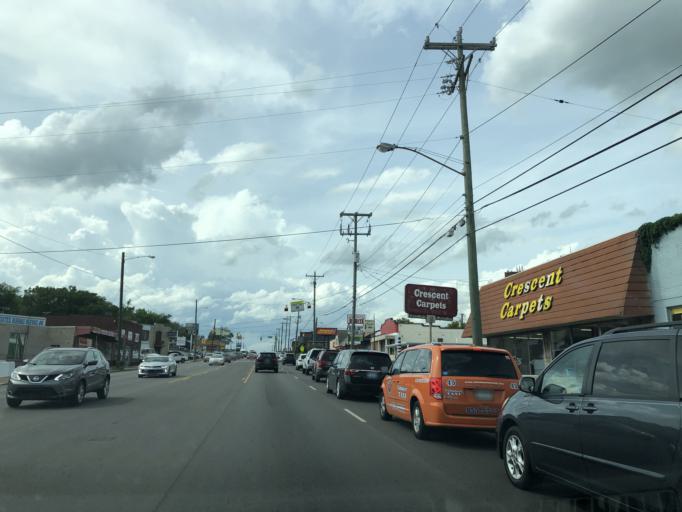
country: US
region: Tennessee
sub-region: Davidson County
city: Oak Hill
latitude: 36.1007
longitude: -86.7400
